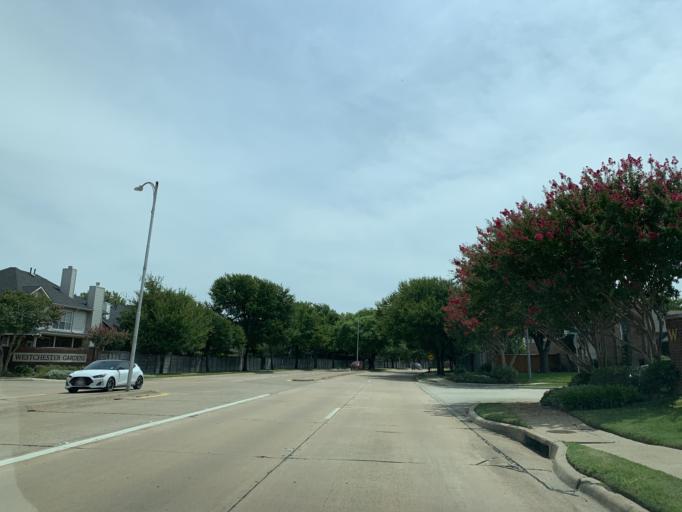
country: US
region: Texas
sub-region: Dallas County
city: Cedar Hill
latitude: 32.6583
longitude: -97.0089
